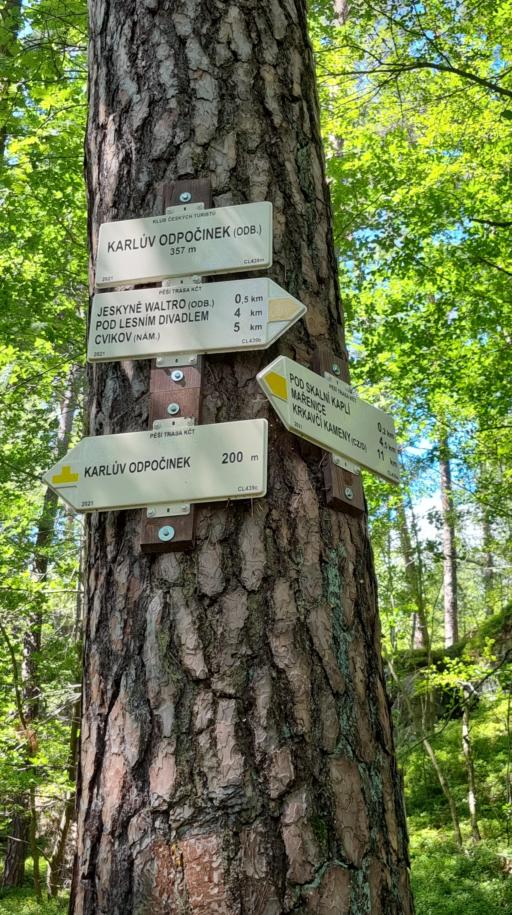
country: CZ
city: Cvikov
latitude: 50.7781
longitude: 14.6708
